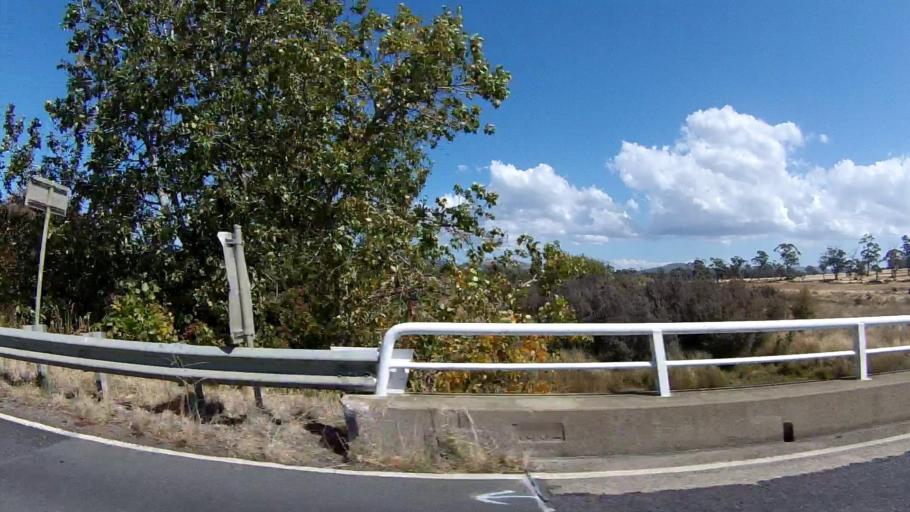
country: AU
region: Tasmania
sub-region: Sorell
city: Sorell
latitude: -42.5948
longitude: 147.7806
